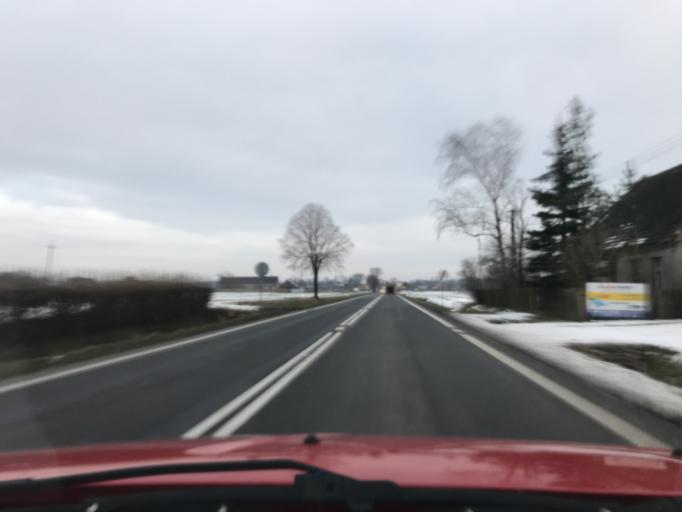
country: PL
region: Greater Poland Voivodeship
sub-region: Powiat pleszewski
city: Pleszew
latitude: 51.8882
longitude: 17.8481
